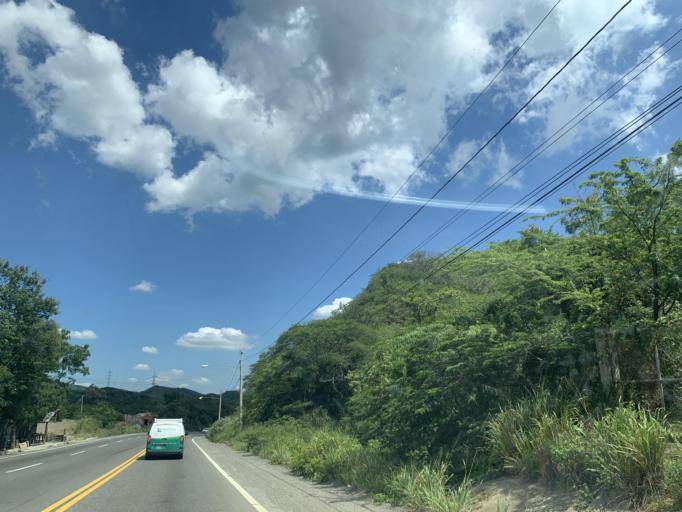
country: DO
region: Santiago
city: Villa Bisono
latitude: 19.6105
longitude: -70.8399
